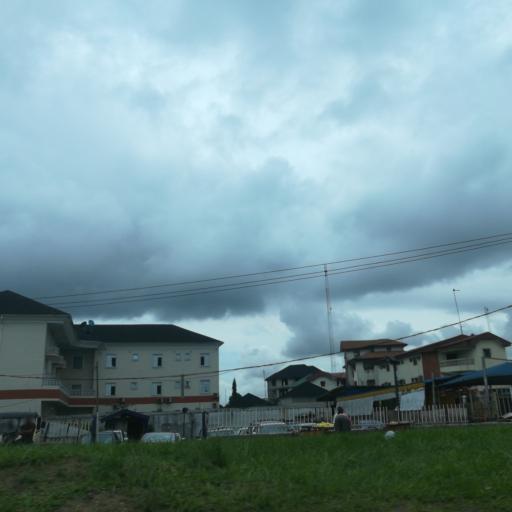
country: NG
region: Rivers
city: Port Harcourt
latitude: 4.8378
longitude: 7.0366
